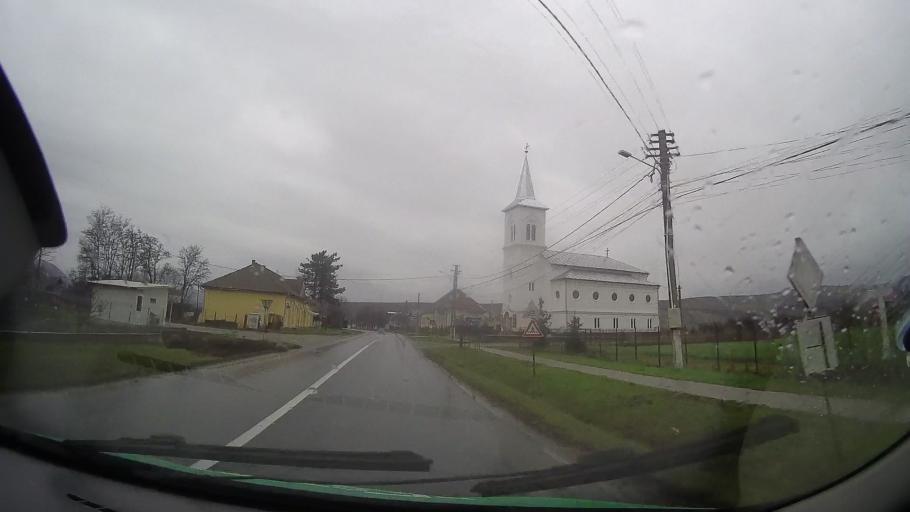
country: RO
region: Bistrita-Nasaud
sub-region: Comuna Mariselu
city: Mariselu
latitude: 47.0357
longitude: 24.4762
